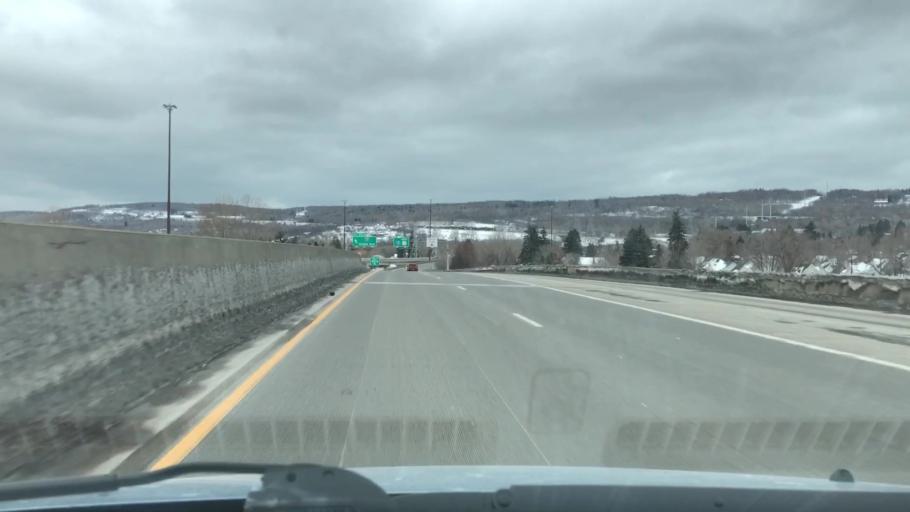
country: US
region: Minnesota
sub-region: Saint Louis County
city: Proctor
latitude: 46.7363
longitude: -92.1704
